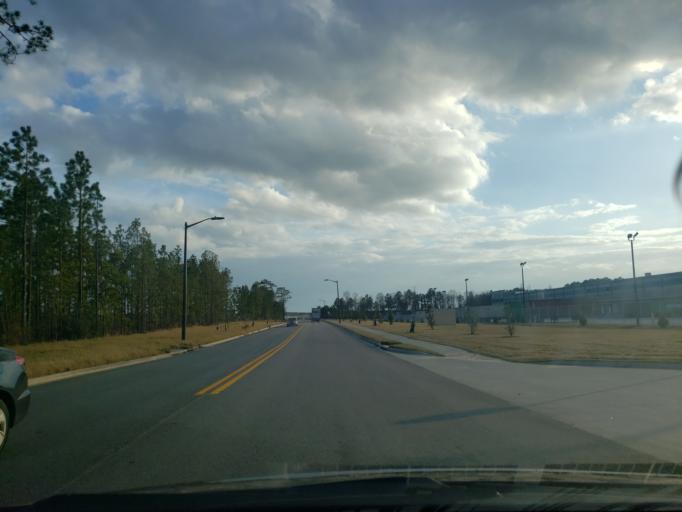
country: US
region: Georgia
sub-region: Chatham County
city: Bloomingdale
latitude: 32.1721
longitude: -81.2700
